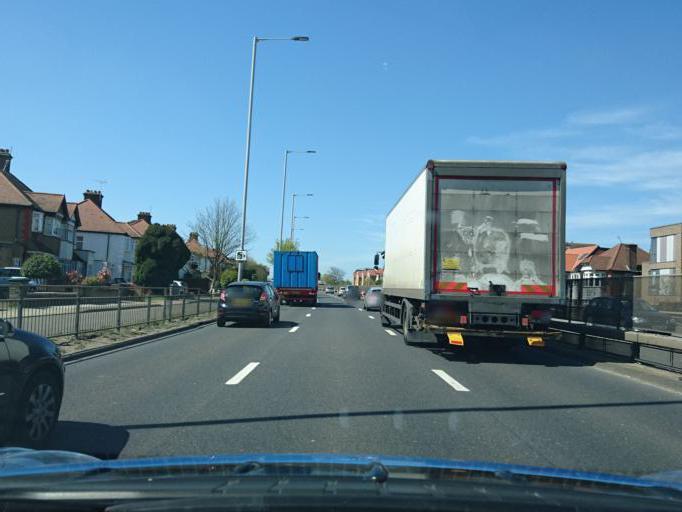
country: GB
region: England
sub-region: Greater London
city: Hendon
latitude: 51.5977
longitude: -0.2216
